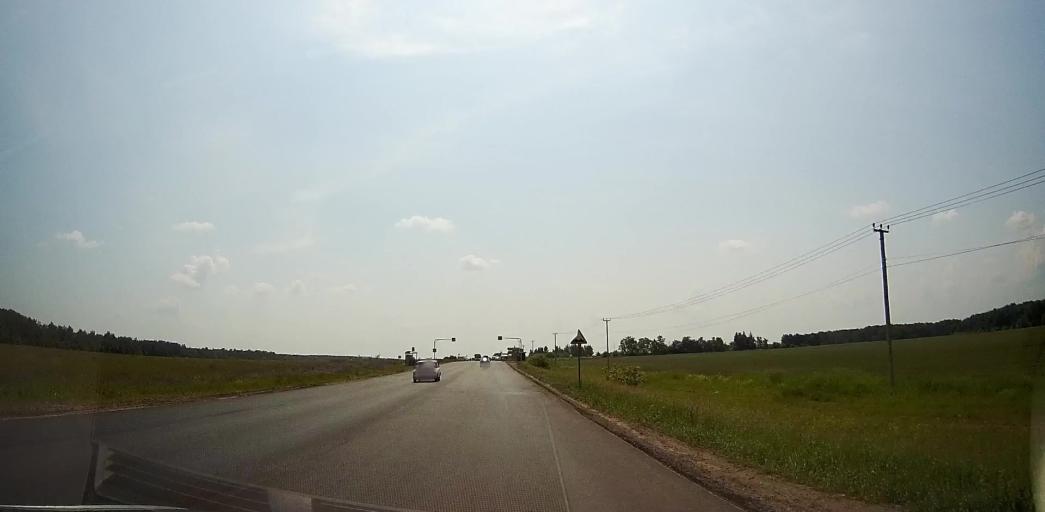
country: RU
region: Moskovskaya
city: Bronnitsy
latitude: 55.2987
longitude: 38.2113
